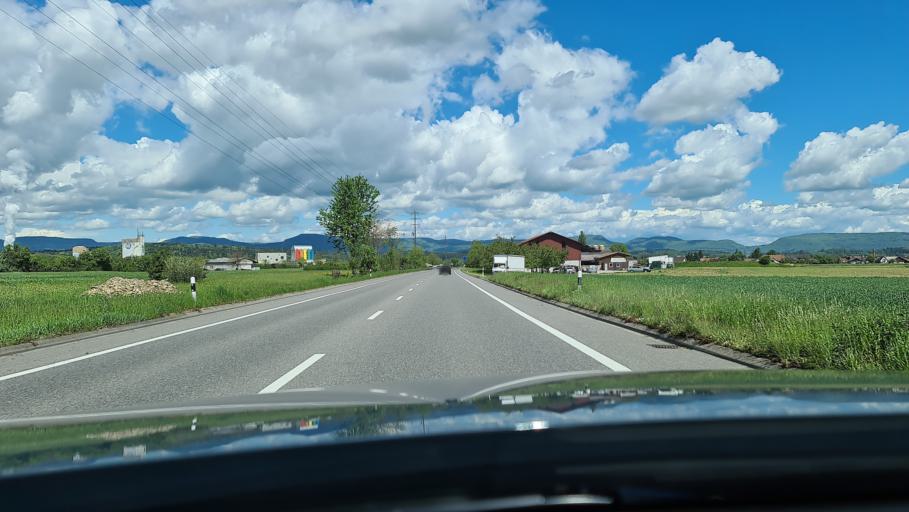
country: CH
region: Aargau
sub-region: Bezirk Aarau
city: Muhen
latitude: 47.3276
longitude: 8.0453
